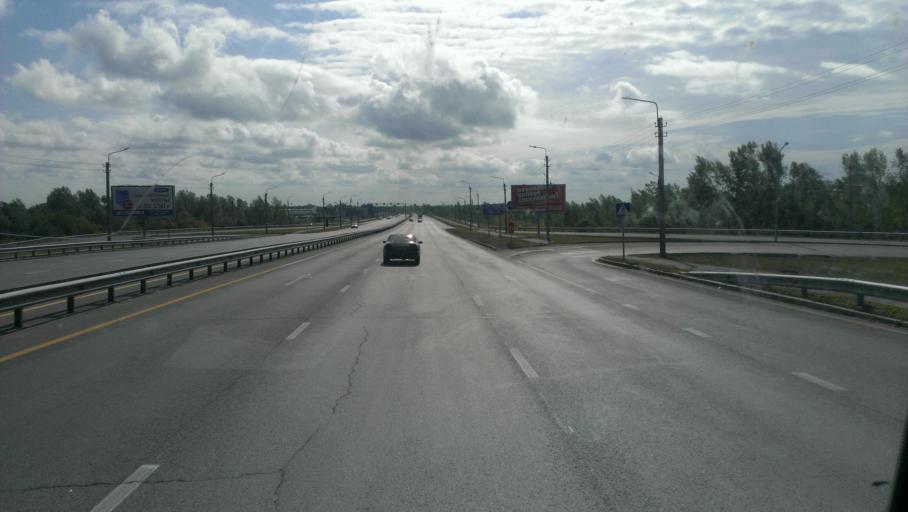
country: RU
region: Altai Krai
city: Zaton
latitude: 53.3199
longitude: 83.8129
